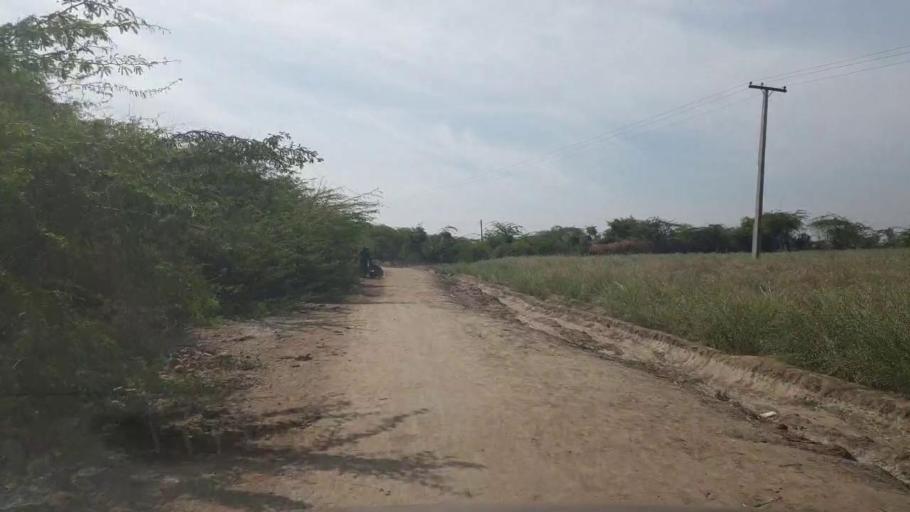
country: PK
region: Sindh
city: Umarkot
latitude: 25.3623
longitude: 69.6186
